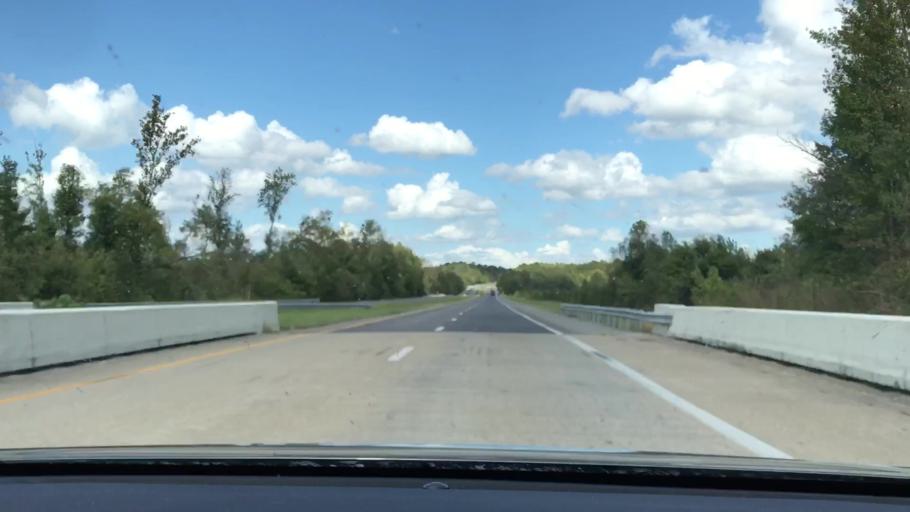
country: US
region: Kentucky
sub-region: Marshall County
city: Benton
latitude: 36.8075
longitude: -88.4927
